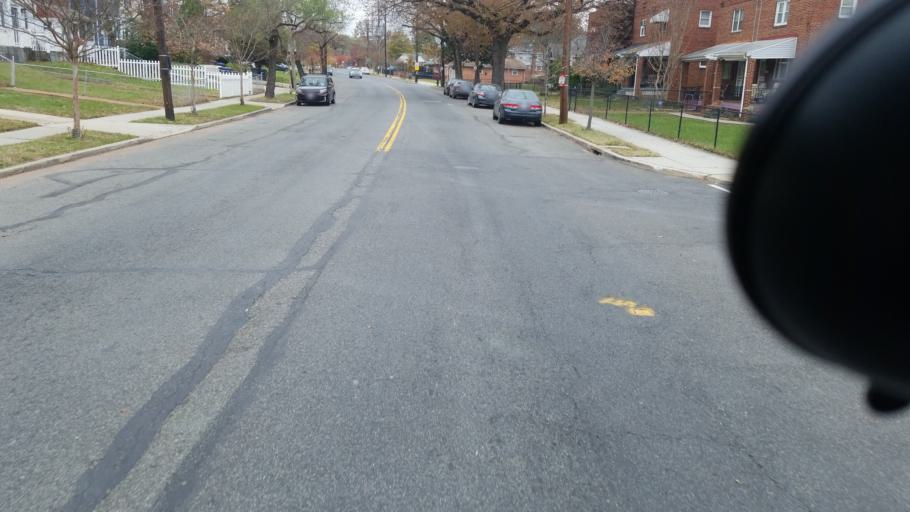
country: US
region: Maryland
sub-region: Prince George's County
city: Capitol Heights
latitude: 38.8863
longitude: -76.9208
